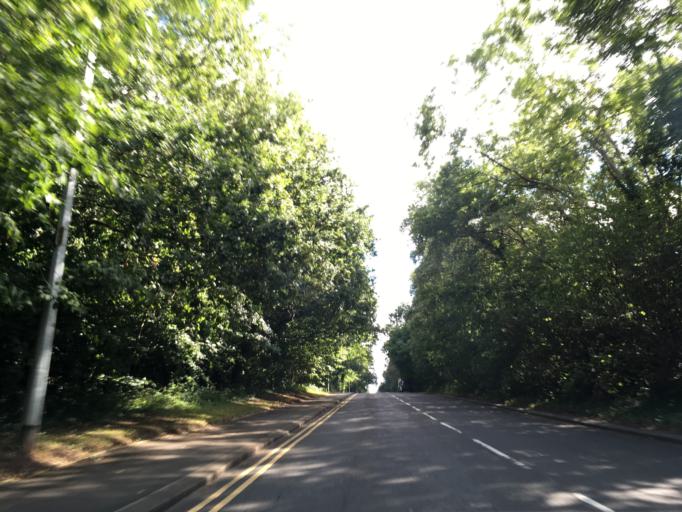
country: GB
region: Wales
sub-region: Cardiff
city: Cardiff
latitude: 51.5129
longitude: -3.1585
